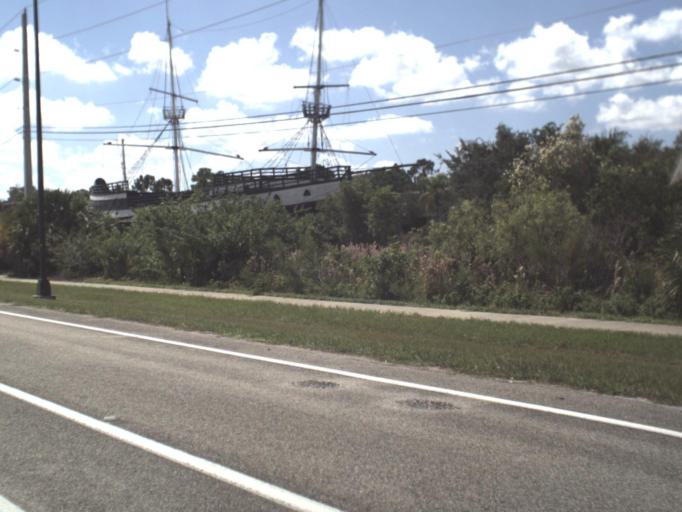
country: US
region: Florida
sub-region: Lee County
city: Estero
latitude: 26.3905
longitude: -81.8099
